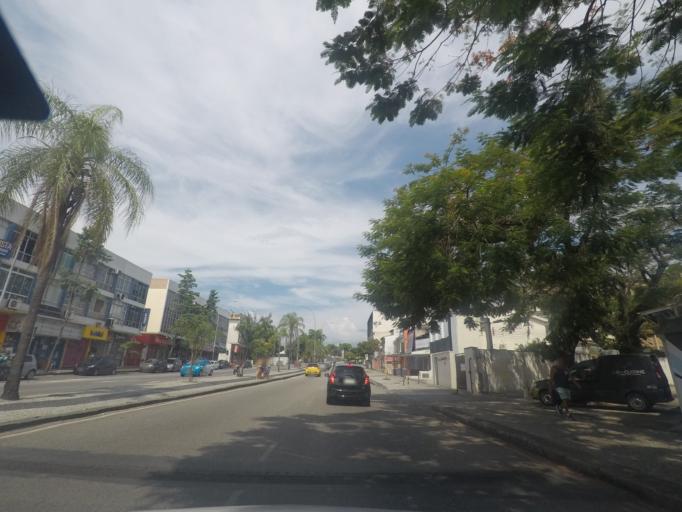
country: BR
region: Rio de Janeiro
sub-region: Rio De Janeiro
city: Rio de Janeiro
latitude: -22.8045
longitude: -43.2058
